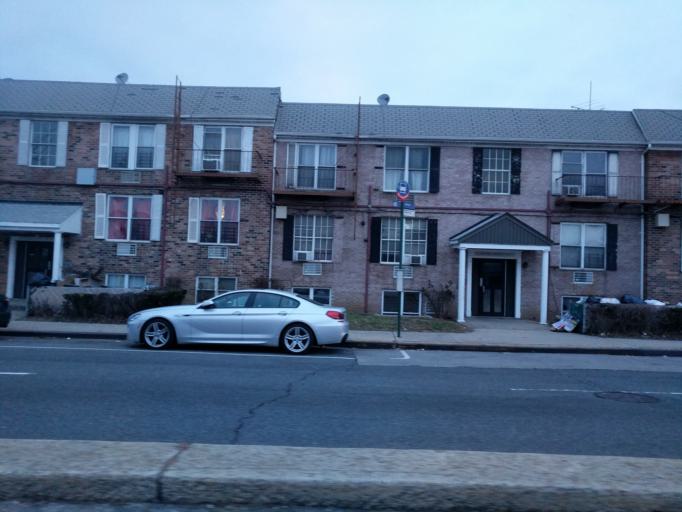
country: US
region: New York
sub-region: Queens County
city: Jamaica
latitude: 40.6826
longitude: -73.7675
